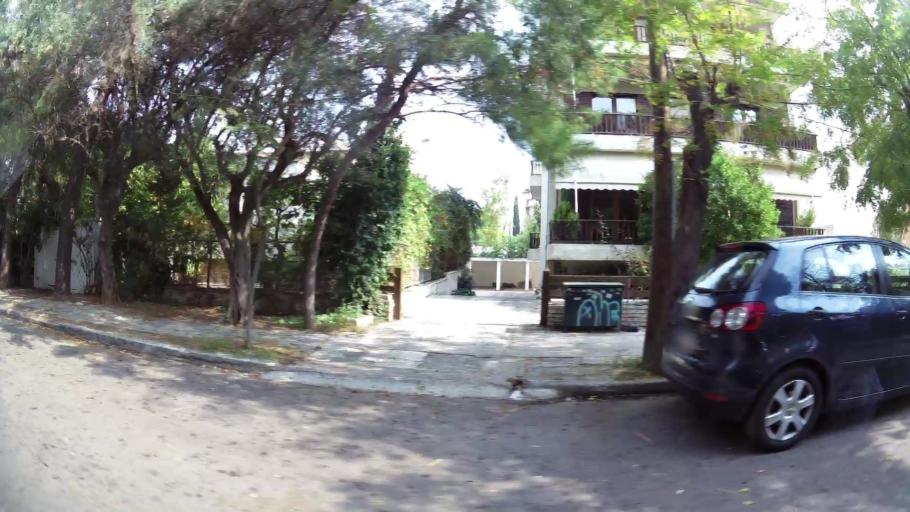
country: GR
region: Attica
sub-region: Nomarchia Athinas
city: Psychiko
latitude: 38.0115
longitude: 23.7787
